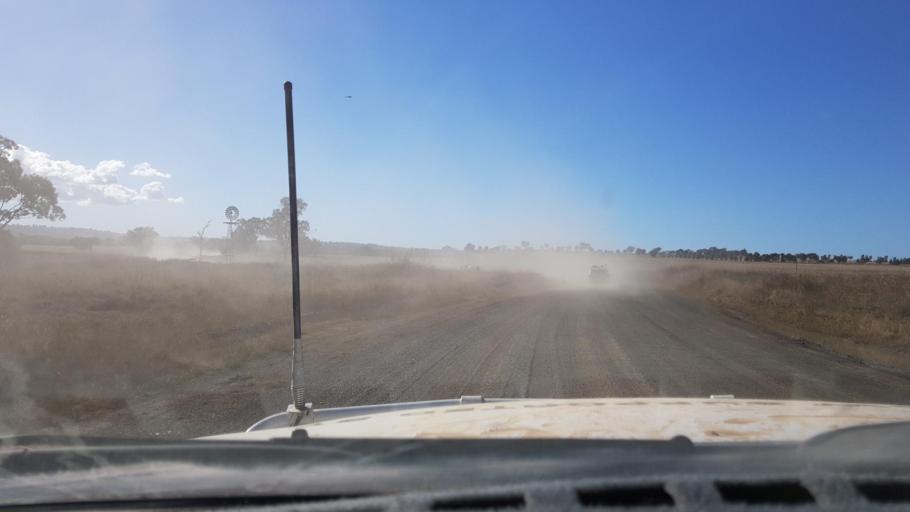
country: AU
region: New South Wales
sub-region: Narrabri
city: Blair Athol
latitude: -30.6747
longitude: 150.4469
